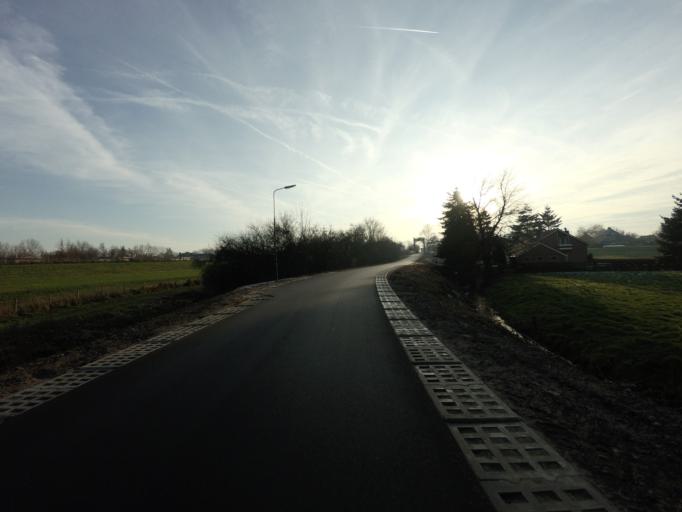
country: NL
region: Utrecht
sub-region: Gemeente De Ronde Venen
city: Mijdrecht
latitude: 52.1983
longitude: 4.8868
